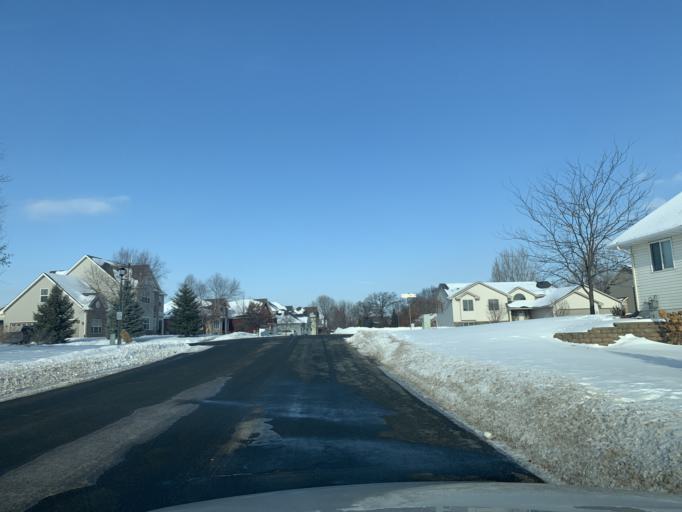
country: US
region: Minnesota
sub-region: Wright County
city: Buffalo
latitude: 45.2015
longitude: -93.8341
